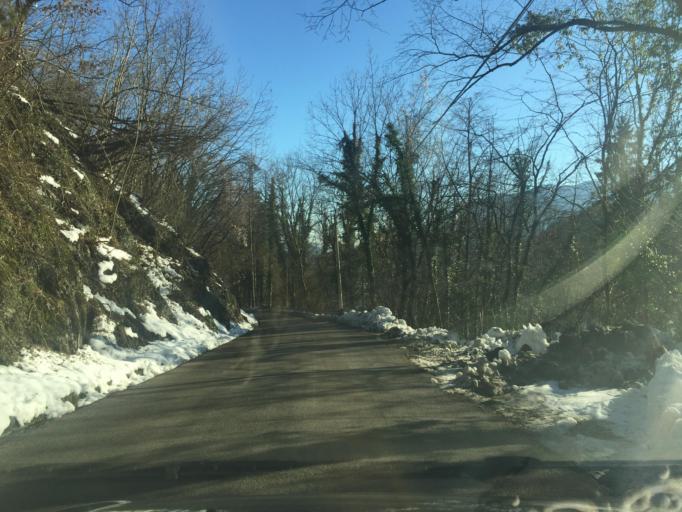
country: IT
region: Friuli Venezia Giulia
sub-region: Provincia di Udine
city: Chiaulis
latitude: 46.4209
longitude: 12.9956
